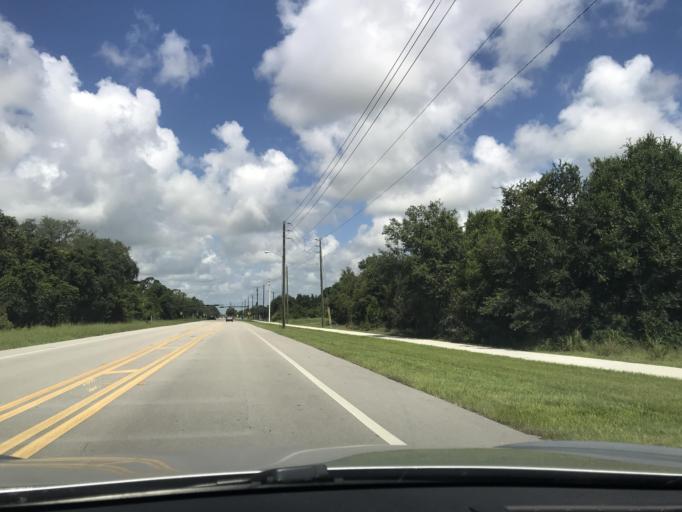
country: US
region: Florida
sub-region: Indian River County
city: Gifford
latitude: 27.6825
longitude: -80.4269
